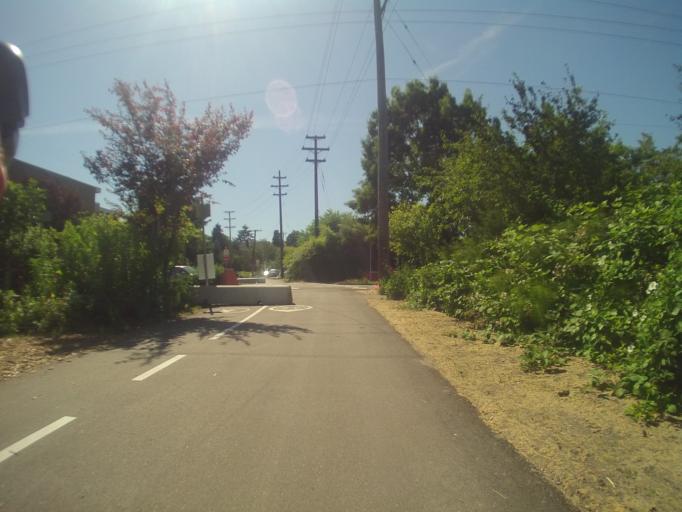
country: CA
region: British Columbia
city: West End
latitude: 49.2665
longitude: -123.1501
